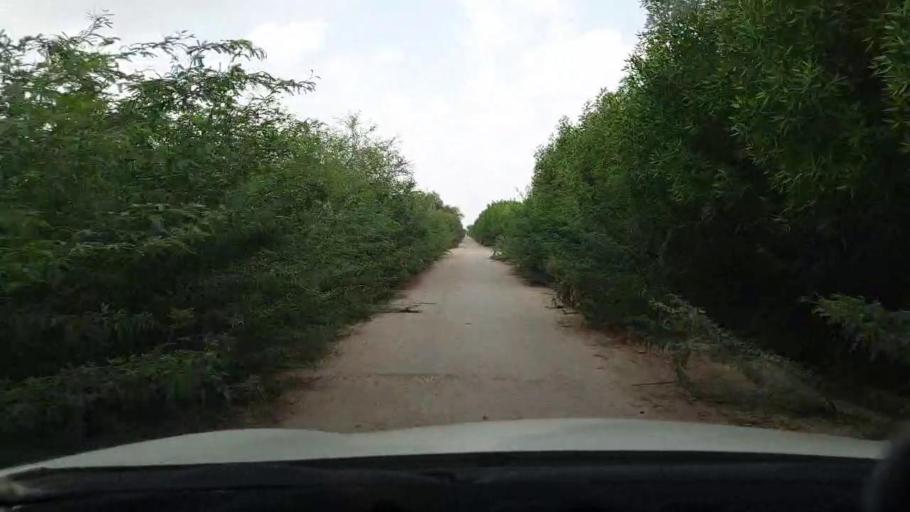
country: PK
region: Sindh
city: Kadhan
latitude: 24.3603
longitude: 68.9609
